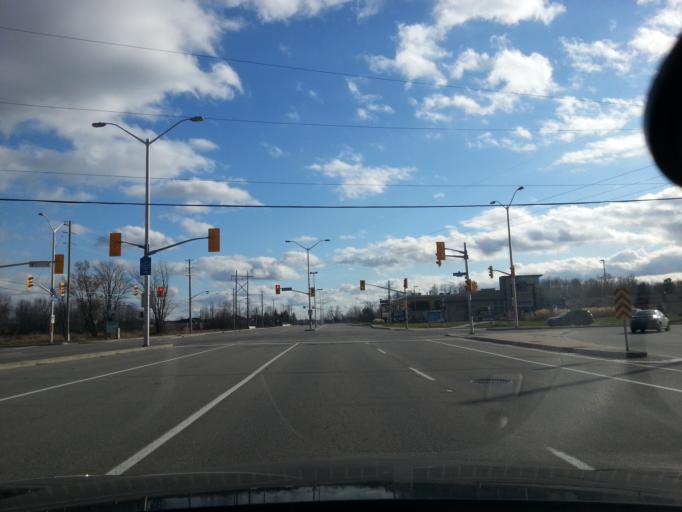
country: CA
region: Ontario
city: Ottawa
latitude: 45.2892
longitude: -75.6721
